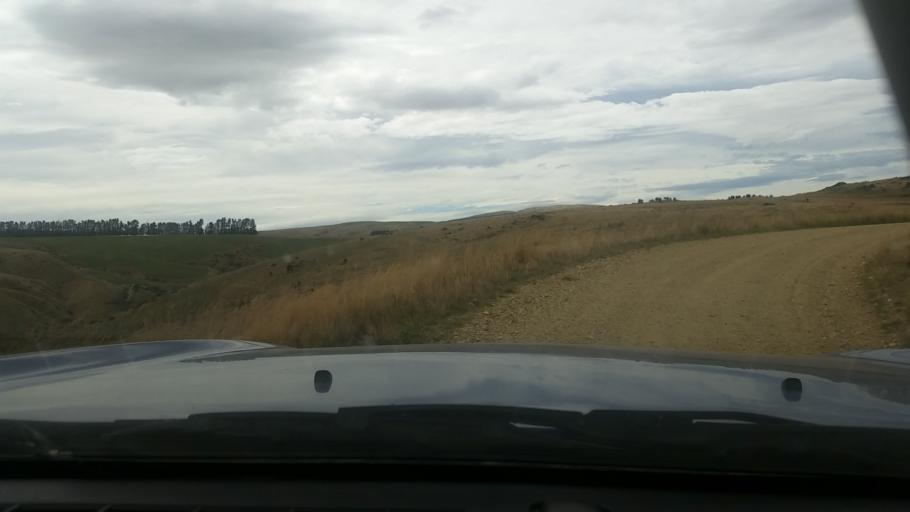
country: NZ
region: Southland
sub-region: Gore District
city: Gore
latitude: -45.5824
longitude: 169.4081
